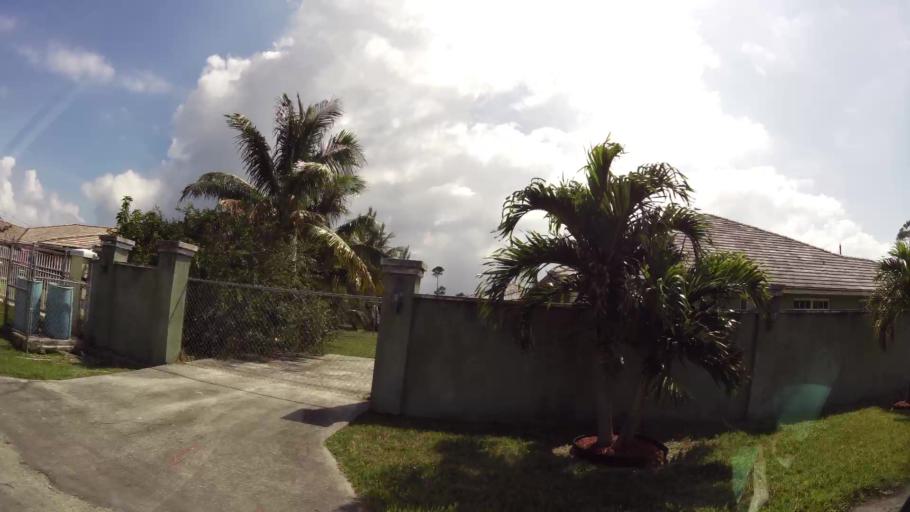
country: BS
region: Freeport
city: Freeport
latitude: 26.5015
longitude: -78.7032
